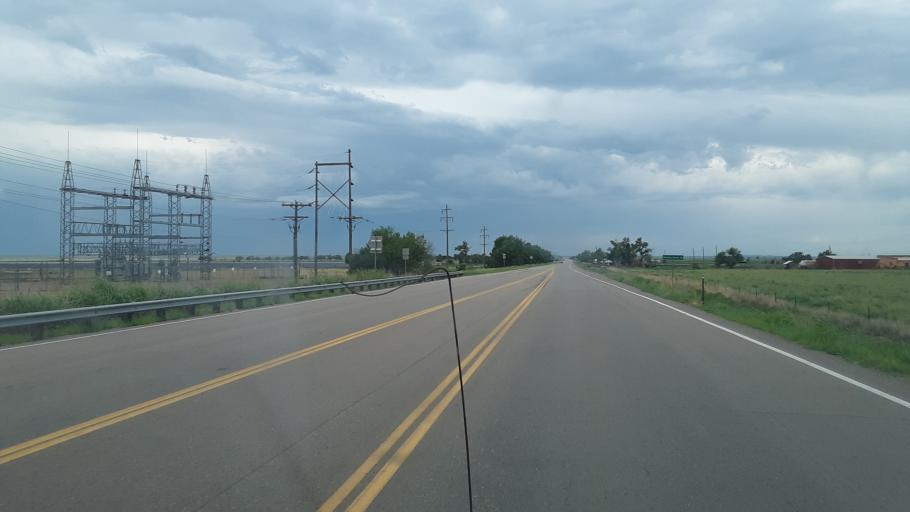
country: US
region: Colorado
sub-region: Crowley County
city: Ordway
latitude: 38.2129
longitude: -103.7485
